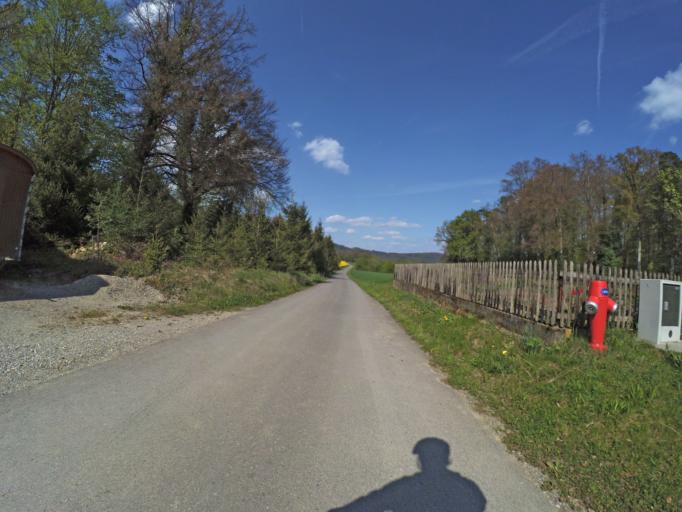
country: CH
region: Thurgau
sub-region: Frauenfeld District
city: Diessenhofen
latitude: 47.6496
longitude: 8.7595
